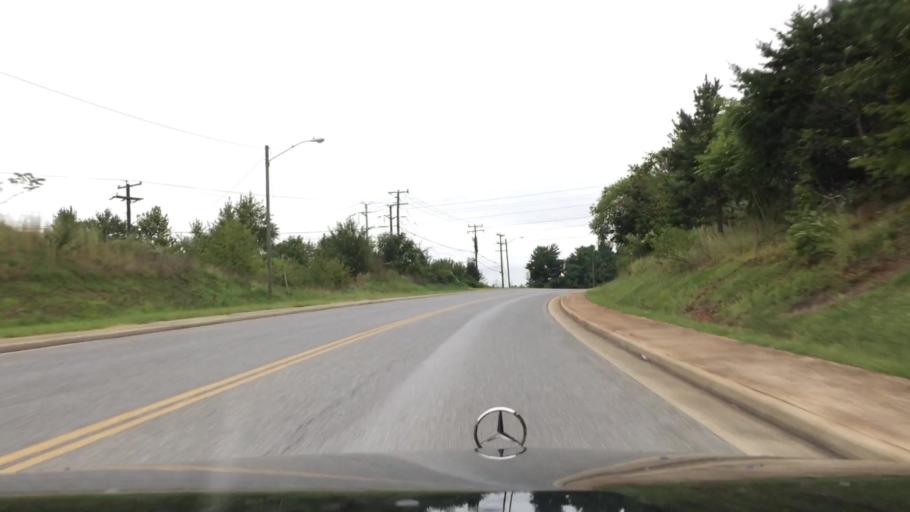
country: US
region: Virginia
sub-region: Campbell County
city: Altavista
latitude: 37.1206
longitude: -79.2762
